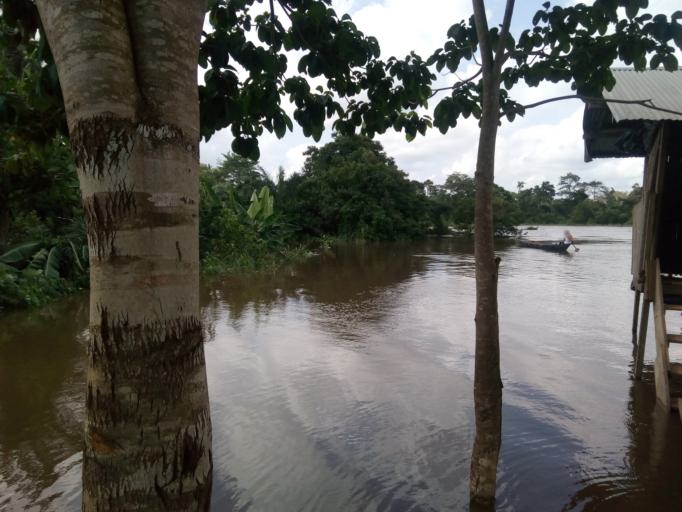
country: CI
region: Sud-Comoe
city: Mafere
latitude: 5.2944
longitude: -2.7844
